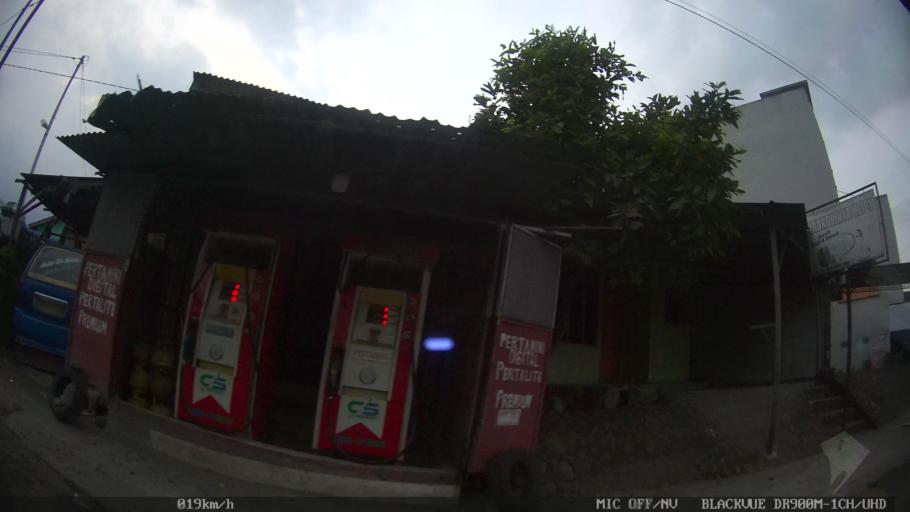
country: ID
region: North Sumatra
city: Sunggal
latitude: 3.5755
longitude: 98.5868
